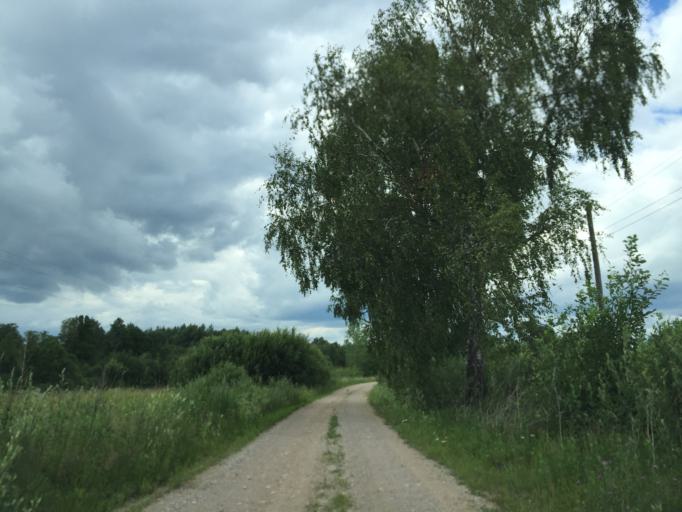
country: LV
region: Ogre
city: Jumprava
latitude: 56.8421
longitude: 25.0531
